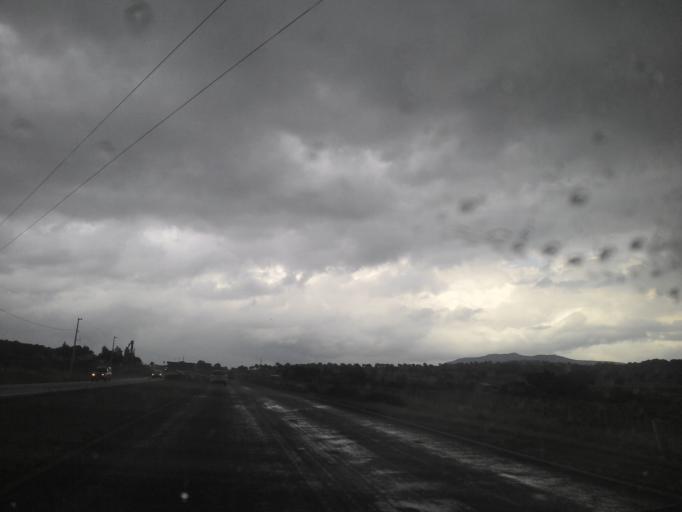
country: MX
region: Hidalgo
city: Zempoala
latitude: 19.9056
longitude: -98.5986
